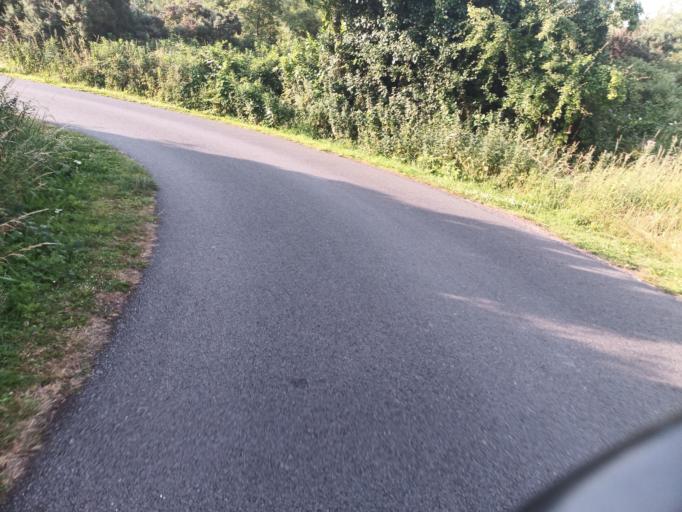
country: GB
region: Northern Ireland
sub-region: Castlereagh District
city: Dundonald
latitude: 54.5895
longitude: -5.8122
